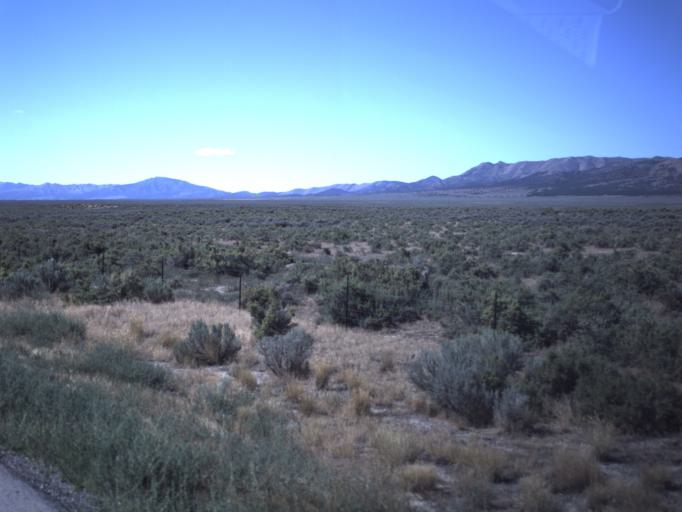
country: US
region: Utah
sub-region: Tooele County
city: Tooele
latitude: 40.2509
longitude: -112.3994
